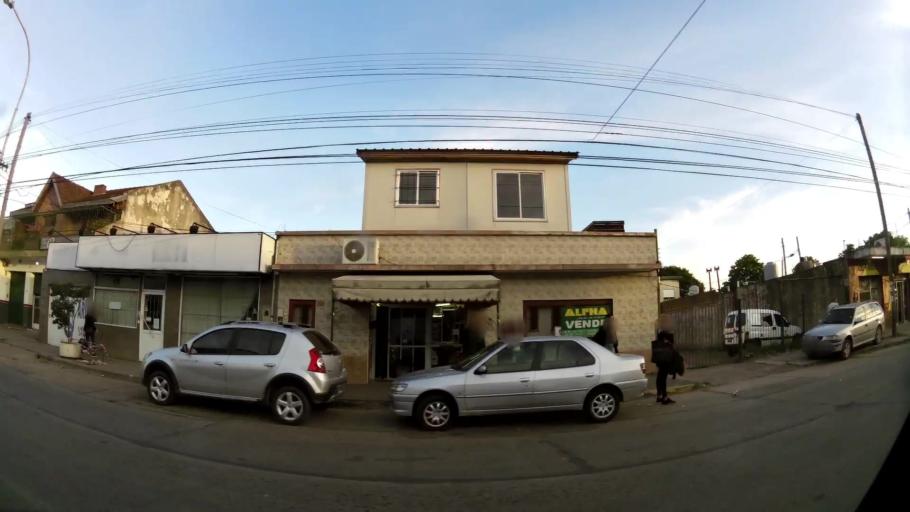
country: AR
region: Buenos Aires
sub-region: Partido de Quilmes
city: Quilmes
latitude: -34.7748
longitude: -58.2338
